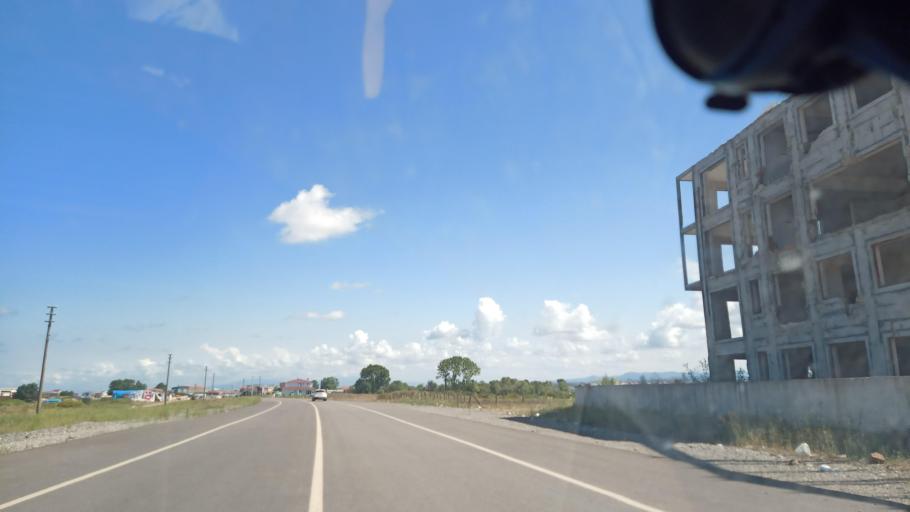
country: TR
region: Sakarya
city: Karasu
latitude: 41.1184
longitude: 30.6587
